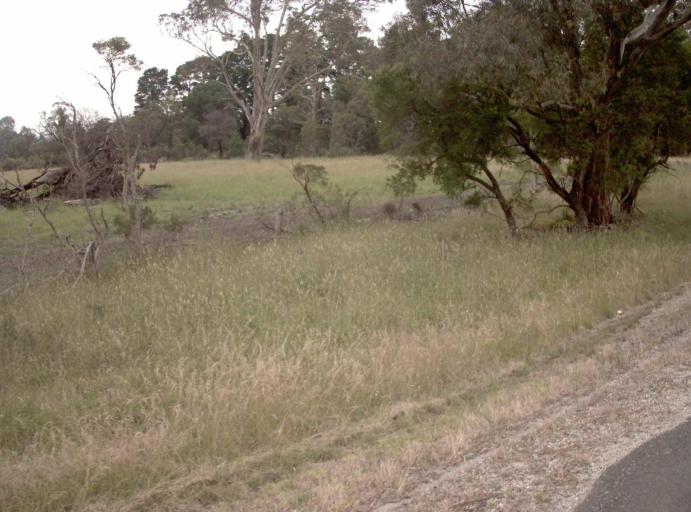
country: AU
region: Victoria
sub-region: Wellington
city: Sale
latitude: -38.1790
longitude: 147.1455
